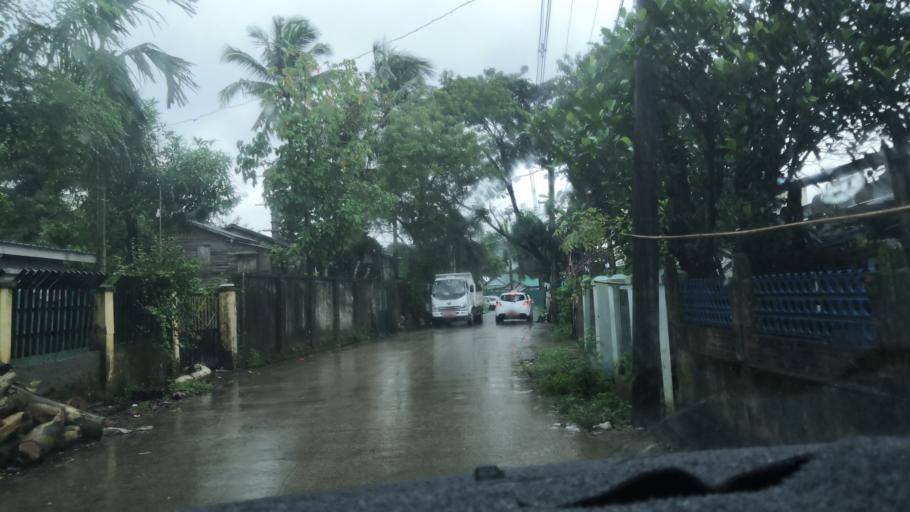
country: MM
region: Yangon
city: Yangon
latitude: 16.8875
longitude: 96.1496
